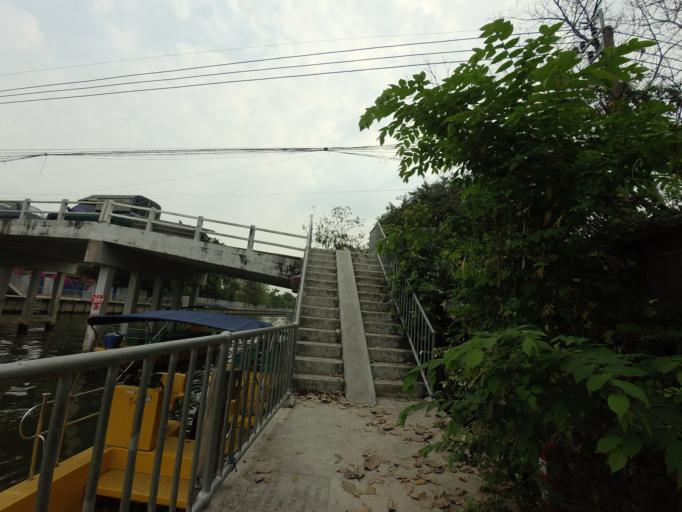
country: TH
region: Bangkok
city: Suan Luang
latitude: 13.7165
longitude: 100.6456
